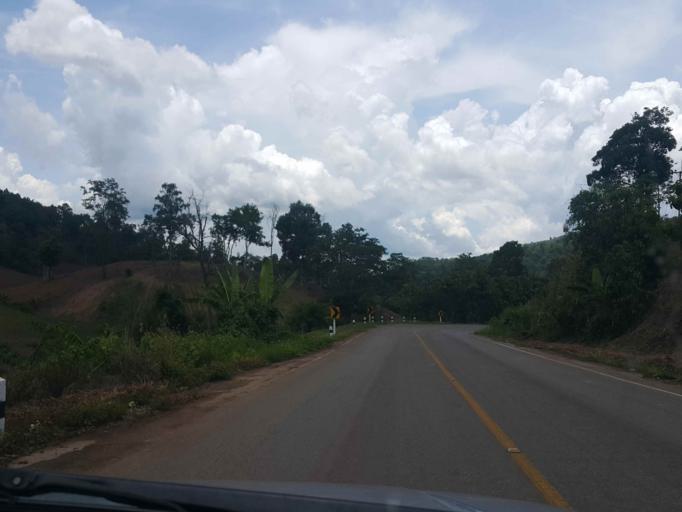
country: TH
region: Phayao
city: Chiang Muan
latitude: 18.9051
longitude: 100.1216
